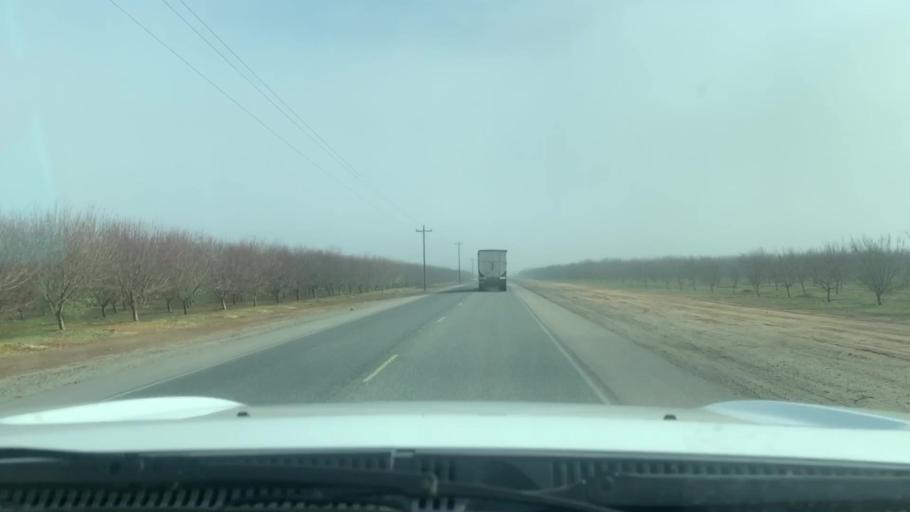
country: US
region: California
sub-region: Kern County
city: Buttonwillow
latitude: 35.5006
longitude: -119.4907
